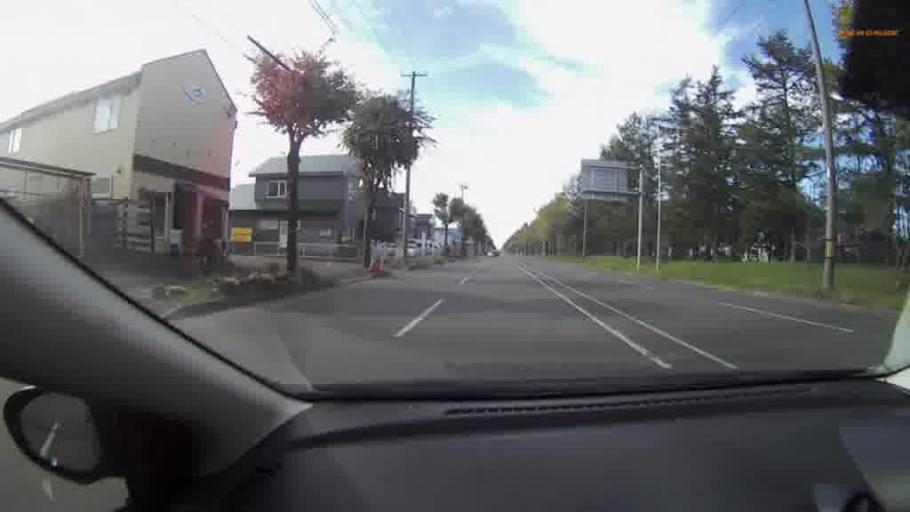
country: JP
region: Hokkaido
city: Kushiro
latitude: 43.0204
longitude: 144.4152
